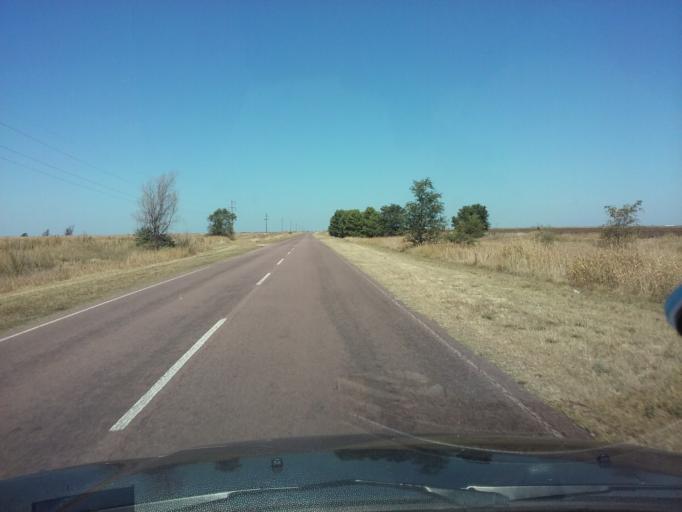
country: AR
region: La Pampa
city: Colonia Baron
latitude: -36.2460
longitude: -63.9428
